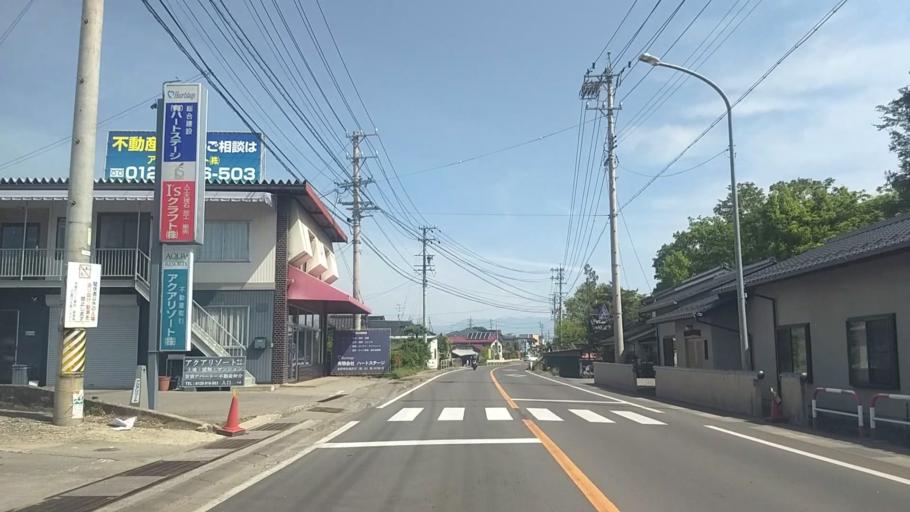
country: JP
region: Nagano
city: Saku
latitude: 36.1808
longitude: 138.4819
